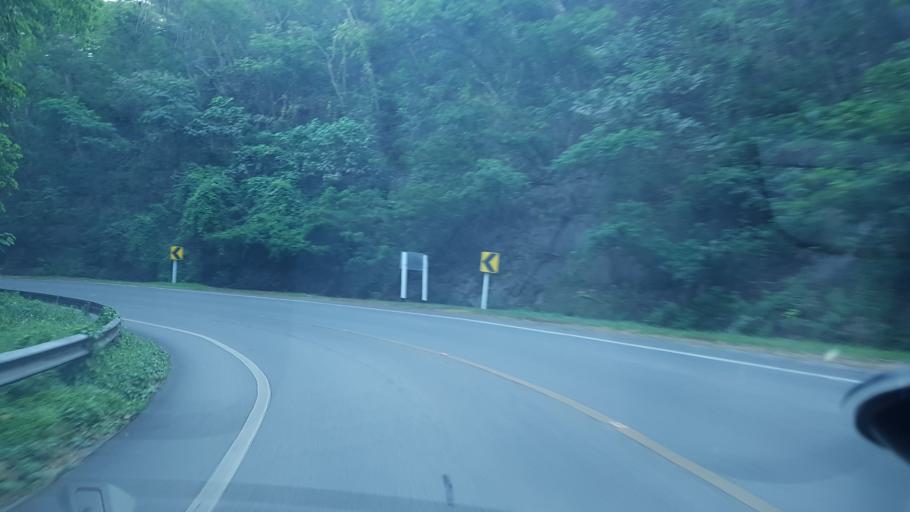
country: TH
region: Chiang Rai
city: Mae Fa Luang
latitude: 20.2958
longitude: 99.8151
